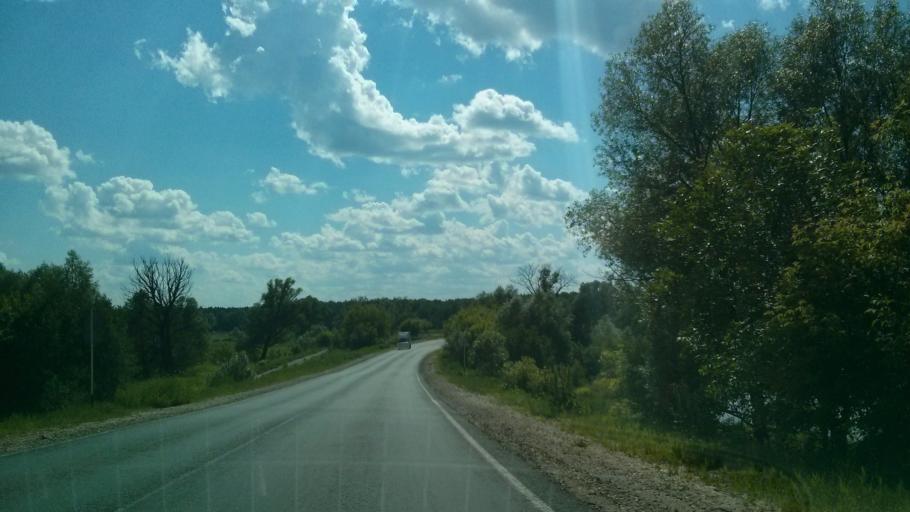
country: RU
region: Vladimir
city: Murom
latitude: 55.5251
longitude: 41.9537
